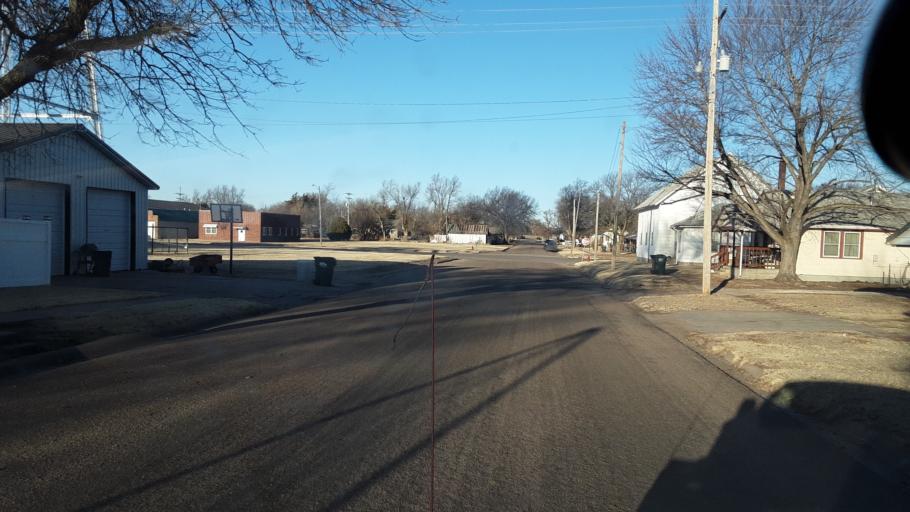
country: US
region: Kansas
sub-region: Rice County
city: Lyons
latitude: 38.3552
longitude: -98.3484
